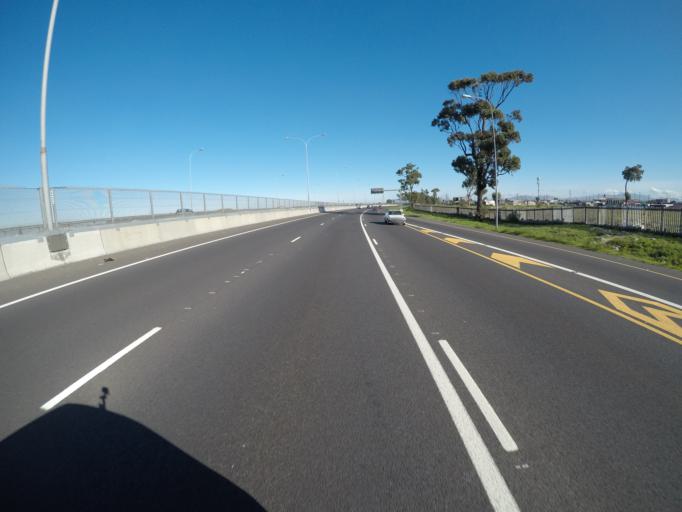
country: ZA
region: Western Cape
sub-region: City of Cape Town
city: Kraaifontein
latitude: -33.9824
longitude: 18.6512
